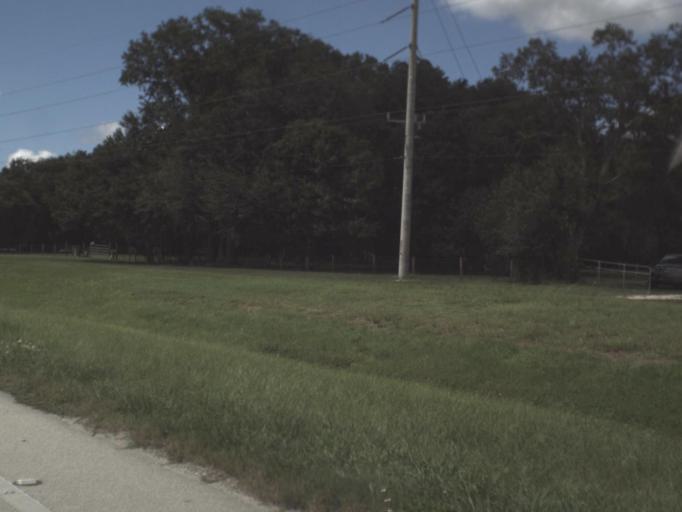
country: US
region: Florida
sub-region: DeSoto County
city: Southeast Arcadia
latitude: 27.2091
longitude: -81.8006
